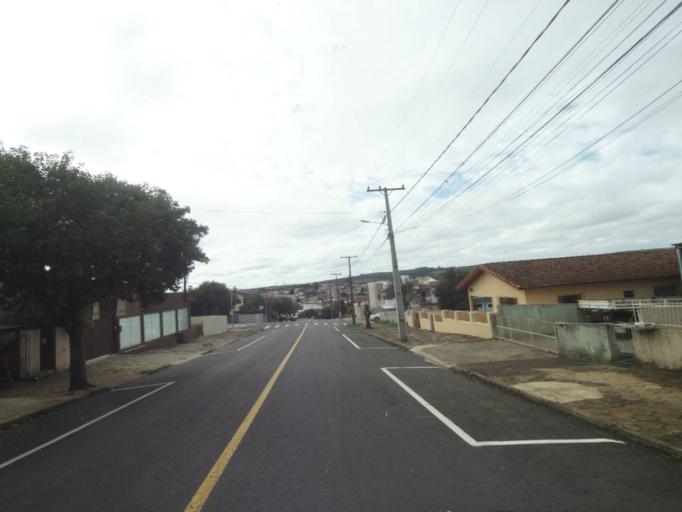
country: BR
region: Parana
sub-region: Telemaco Borba
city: Telemaco Borba
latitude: -24.3324
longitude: -50.6191
